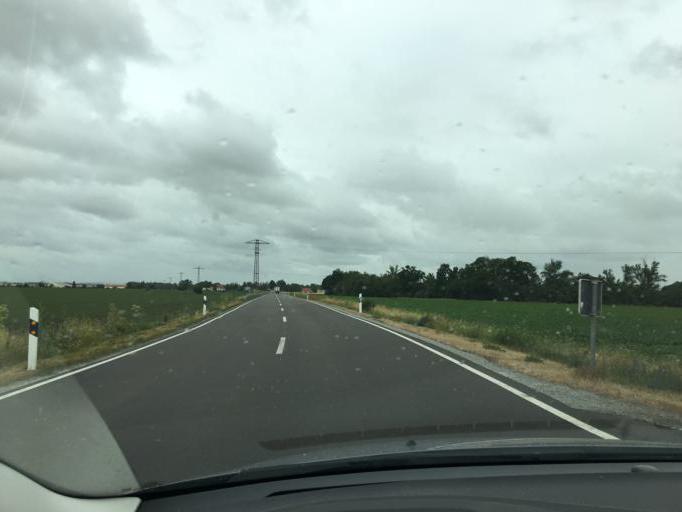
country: DE
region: Saxony-Anhalt
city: Glothe
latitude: 51.8969
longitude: 11.6847
